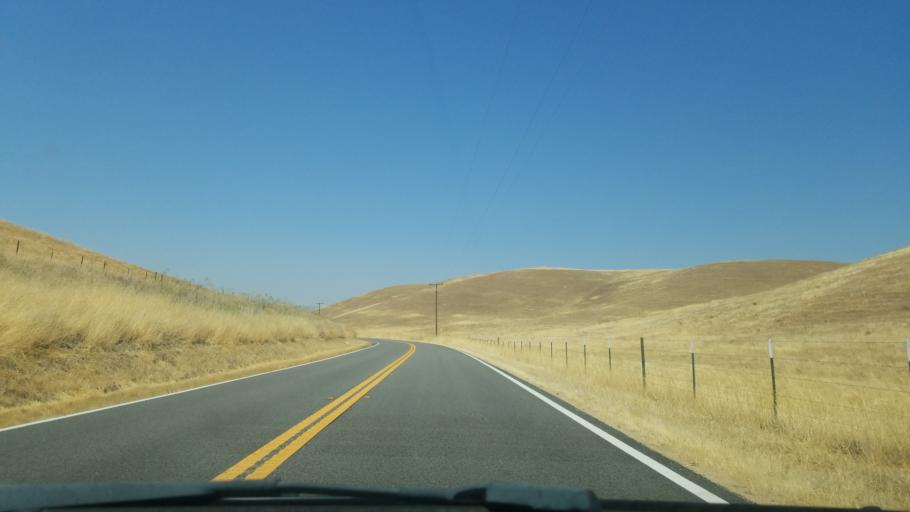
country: US
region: California
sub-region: San Luis Obispo County
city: Shandon
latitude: 35.6063
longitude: -120.4080
